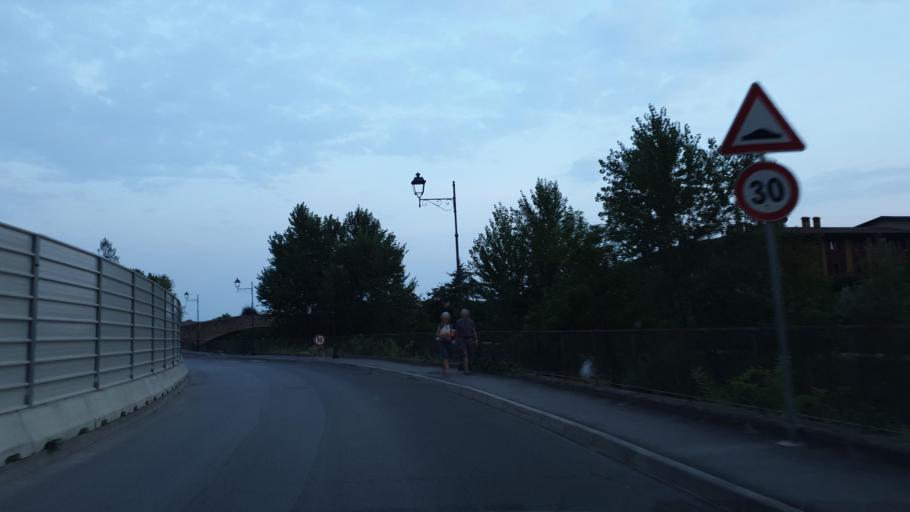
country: IT
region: Lombardy
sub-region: Provincia di Brescia
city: Toscolano Maderno
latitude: 45.6373
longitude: 10.6105
